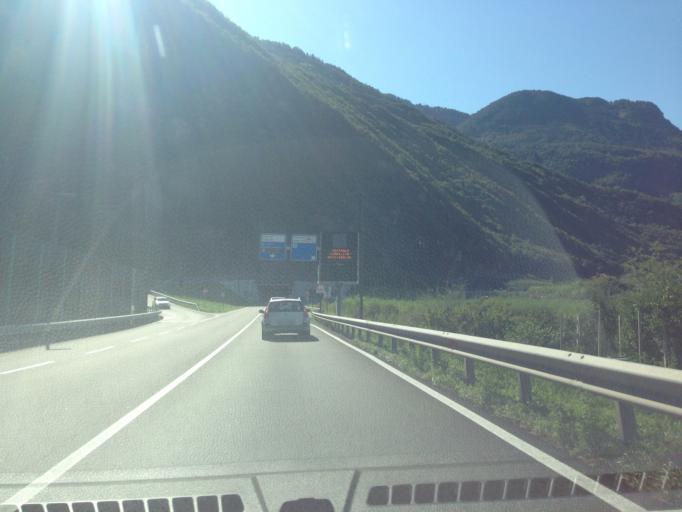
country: IT
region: Trentino-Alto Adige
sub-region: Bolzano
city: Pineta
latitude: 46.4360
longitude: 11.3453
